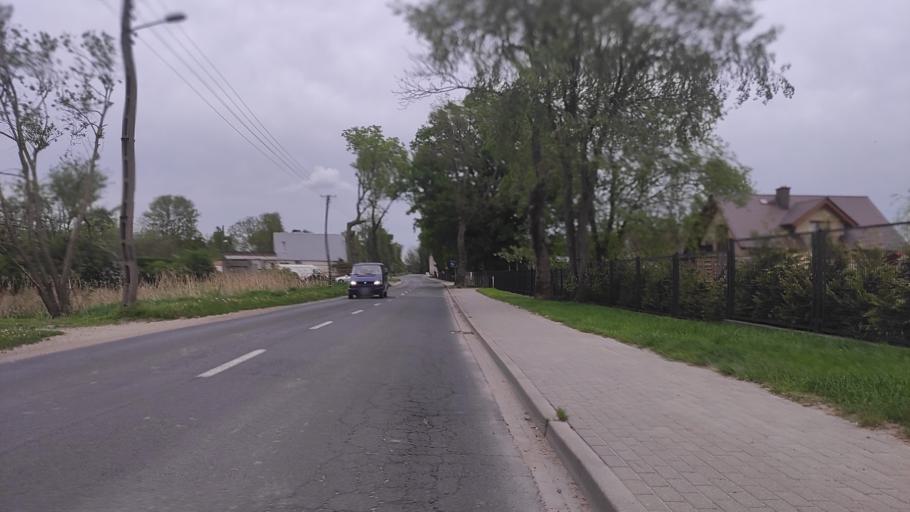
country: PL
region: Greater Poland Voivodeship
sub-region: Powiat poznanski
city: Swarzedz
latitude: 52.4128
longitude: 17.1182
